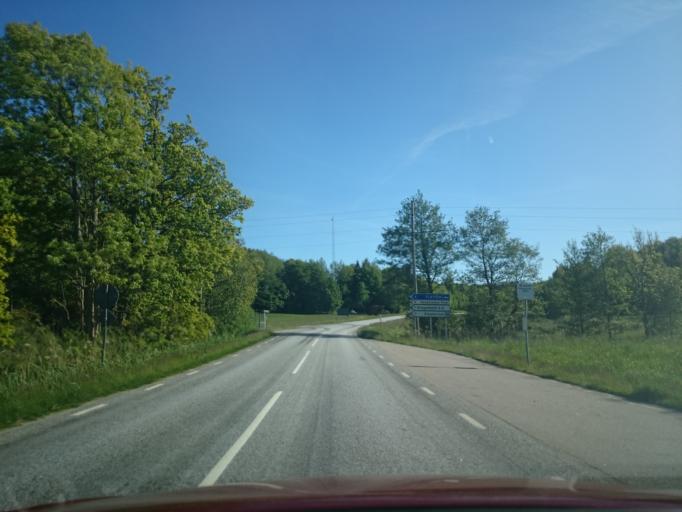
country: SE
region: Vaestra Goetaland
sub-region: Lysekils Kommun
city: Lysekil
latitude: 58.2629
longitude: 11.5379
